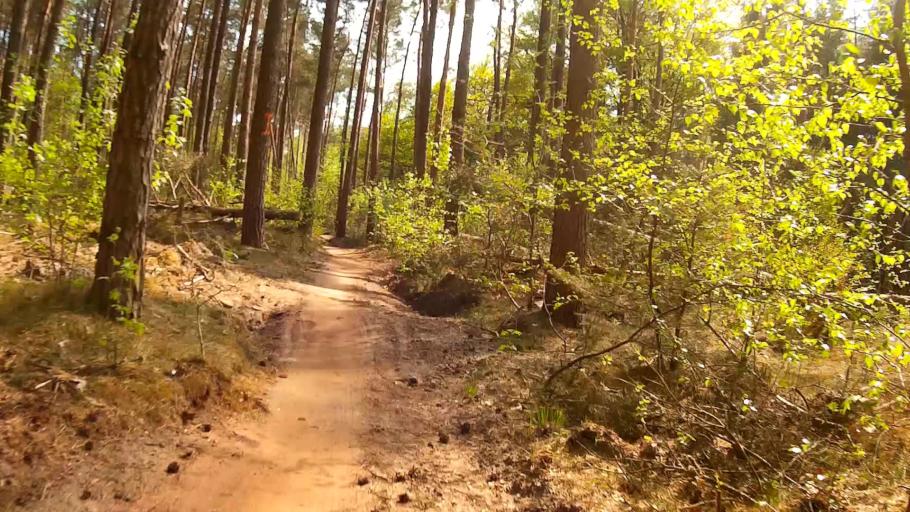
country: NL
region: Utrecht
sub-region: Gemeente Baarn
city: Baarn
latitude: 52.1875
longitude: 5.2382
